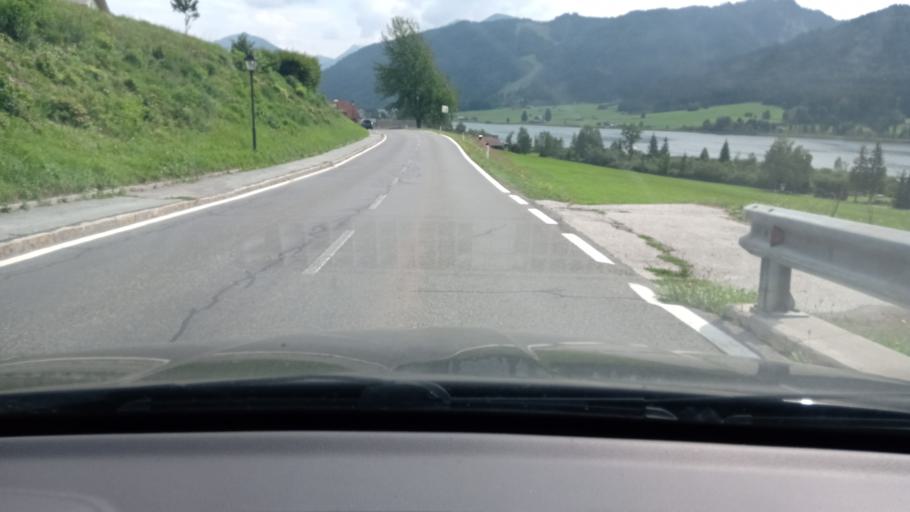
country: AT
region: Carinthia
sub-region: Politischer Bezirk Spittal an der Drau
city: Steinfeld
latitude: 46.7216
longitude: 13.2757
